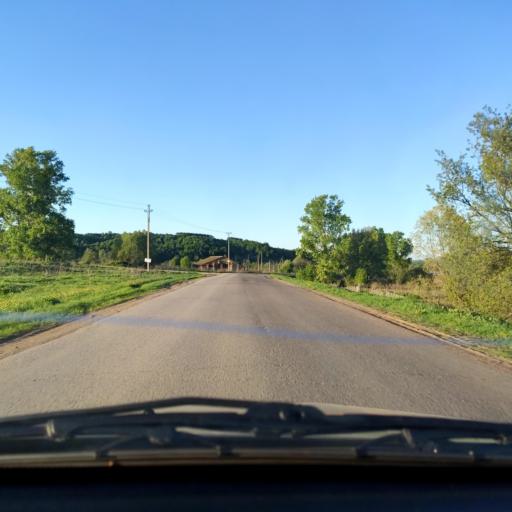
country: RU
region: Bashkortostan
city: Yazykovo
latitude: 55.0470
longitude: 56.1668
